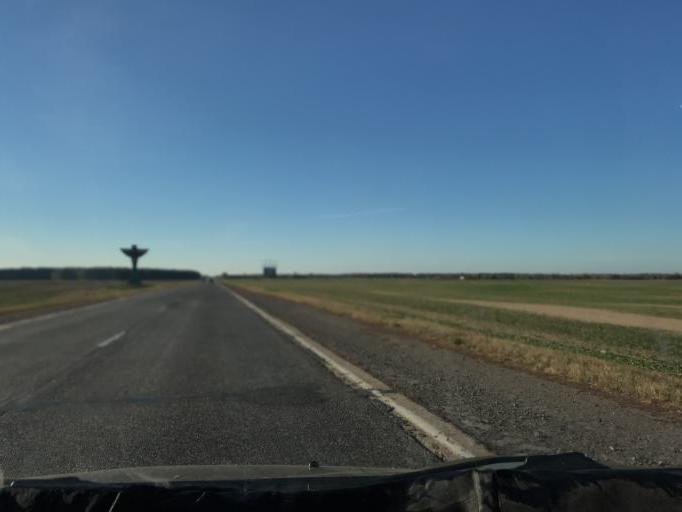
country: BY
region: Gomel
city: Mazyr
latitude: 52.2218
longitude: 29.0028
